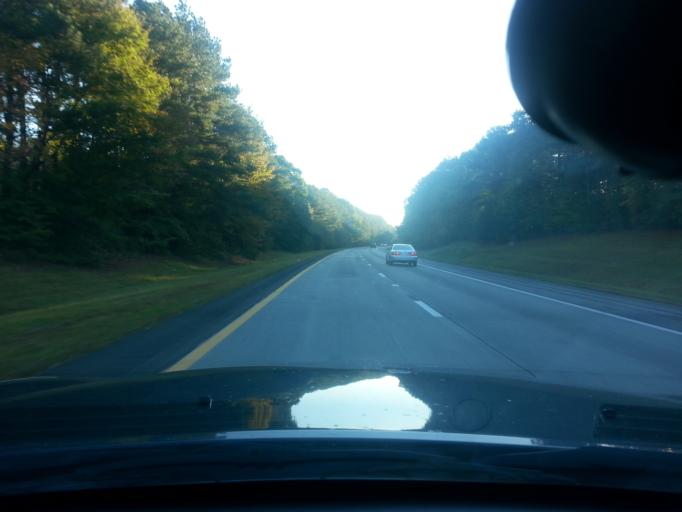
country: US
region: North Carolina
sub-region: Granville County
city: Oxford
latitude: 36.3208
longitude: -78.5247
